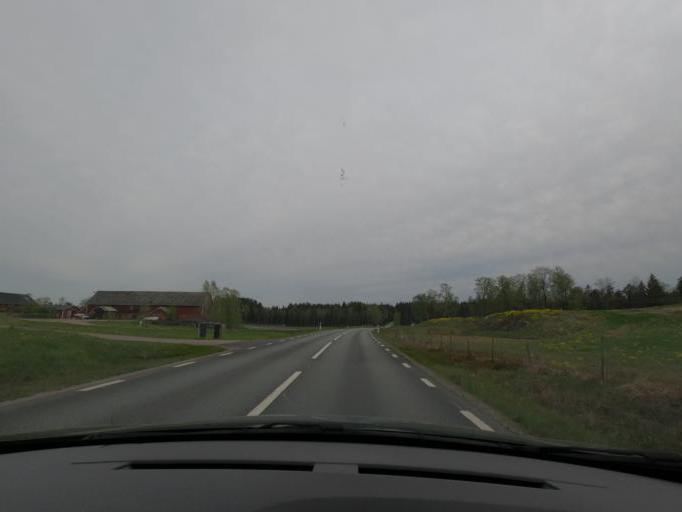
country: SE
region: Joenkoeping
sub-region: Varnamo Kommun
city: Bredaryd
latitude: 57.2002
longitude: 13.7626
